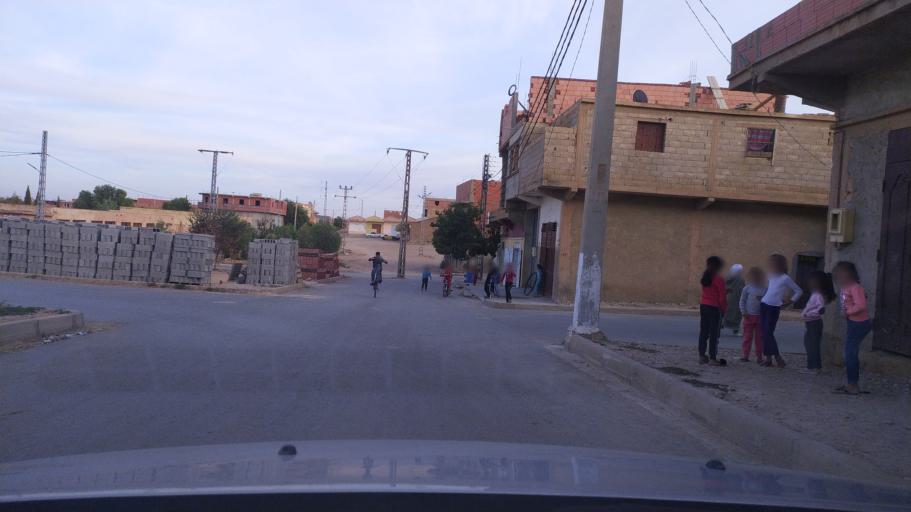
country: DZ
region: Tiaret
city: Frenda
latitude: 34.8933
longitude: 1.2409
